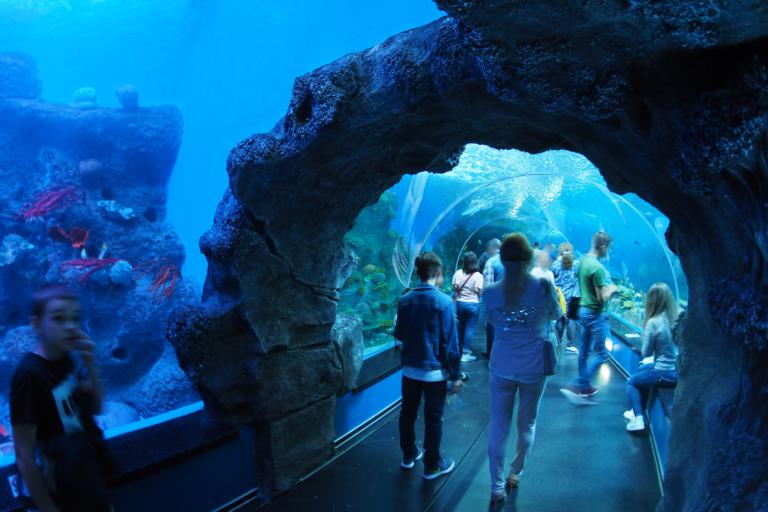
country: RU
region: Primorskiy
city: Russkiy
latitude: 43.0141
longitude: 131.9302
